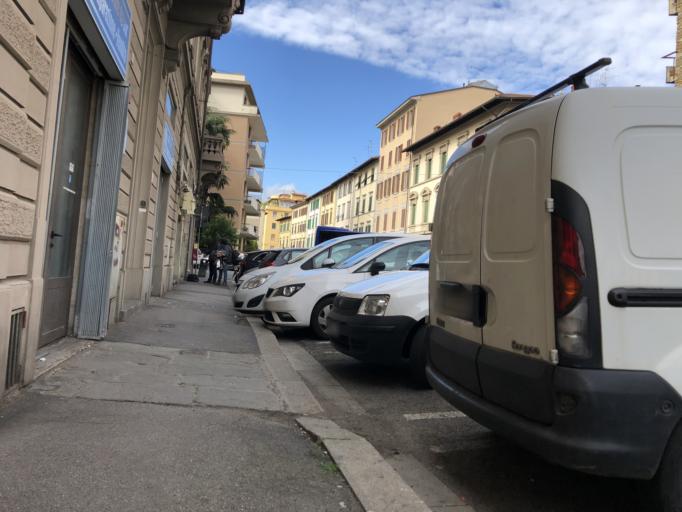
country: IT
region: Tuscany
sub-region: Province of Florence
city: Florence
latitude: 43.7739
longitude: 11.2741
